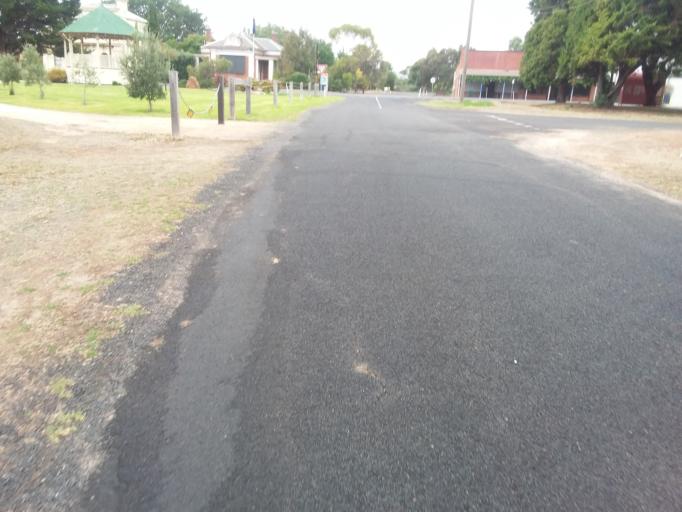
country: AU
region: Victoria
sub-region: Horsham
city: Horsham
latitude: -36.7416
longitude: 141.9410
